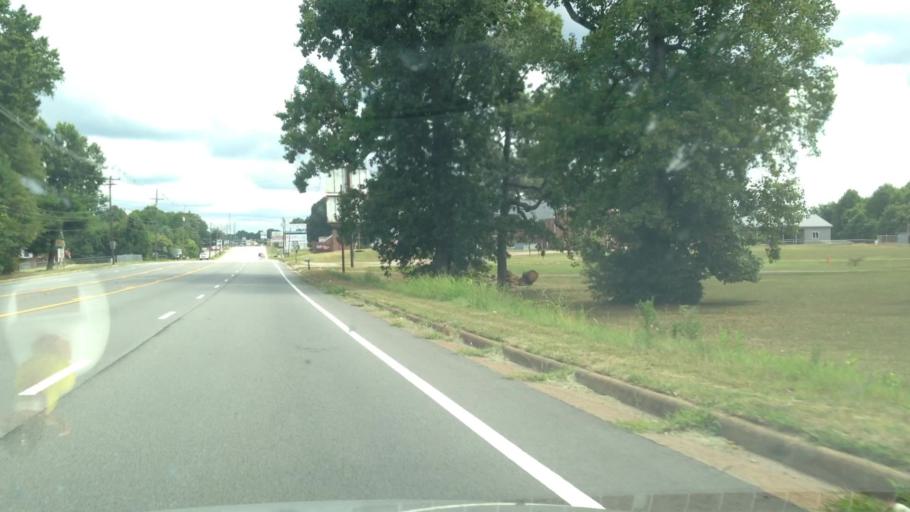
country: US
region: Virginia
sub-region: Pittsylvania County
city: Mount Hermon
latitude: 36.6818
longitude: -79.3716
